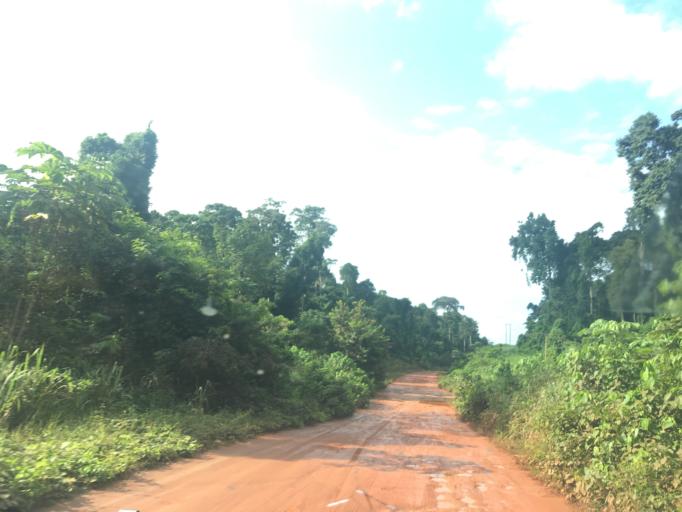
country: GH
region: Western
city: Wassa-Akropong
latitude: 5.9678
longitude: -2.4211
